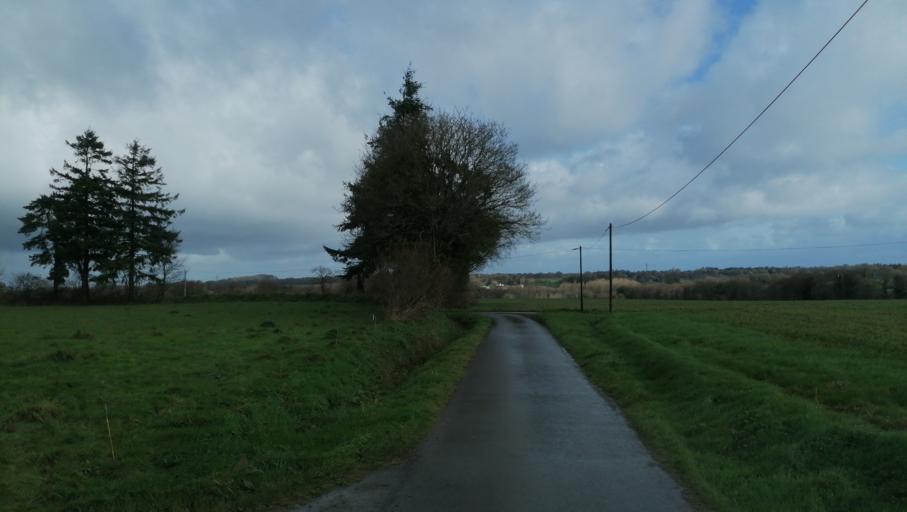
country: FR
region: Brittany
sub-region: Departement des Cotes-d'Armor
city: Lanrodec
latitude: 48.4839
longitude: -3.0390
